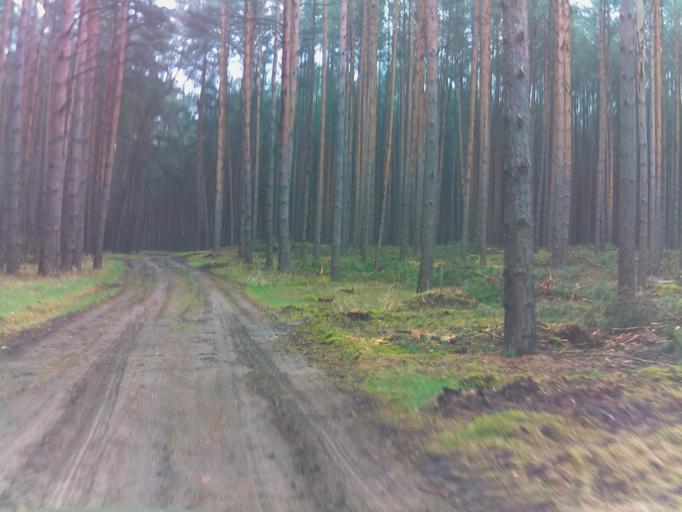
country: DE
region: Brandenburg
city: Schlepzig
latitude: 52.0147
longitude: 13.9861
